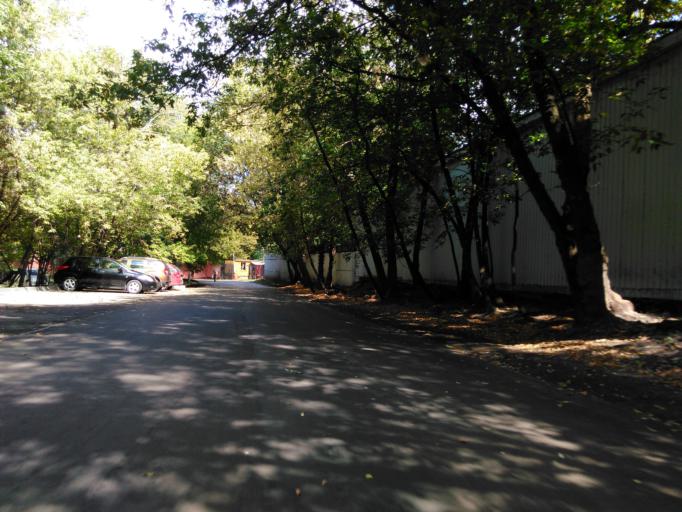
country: RU
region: Moscow
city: Novyye Cheremushki
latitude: 55.6949
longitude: 37.6144
